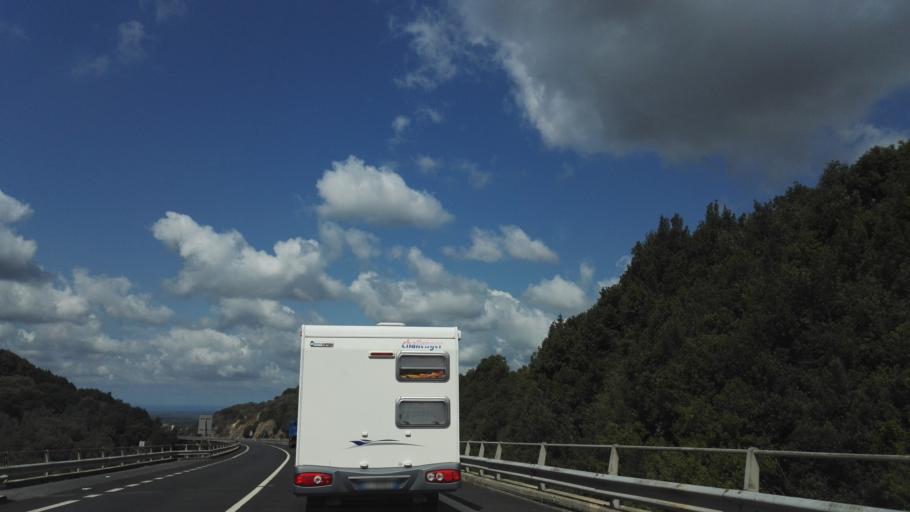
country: IT
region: Calabria
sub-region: Provincia di Reggio Calabria
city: Anoia Superiore
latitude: 38.4170
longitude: 16.1243
